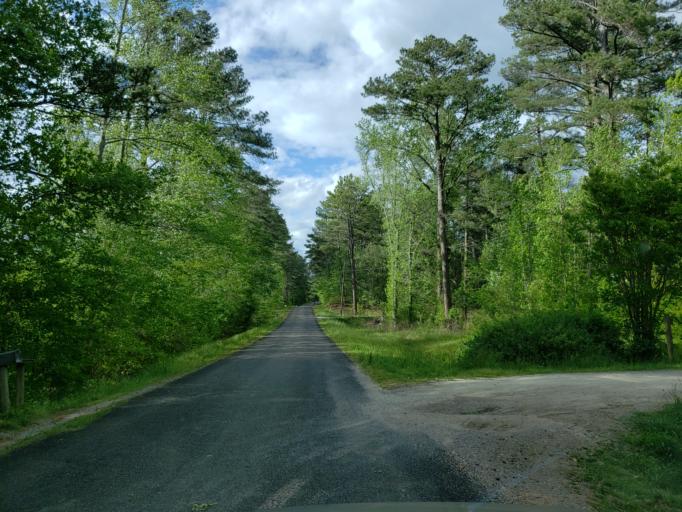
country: US
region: Georgia
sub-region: Haralson County
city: Tallapoosa
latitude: 33.7811
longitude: -85.3814
